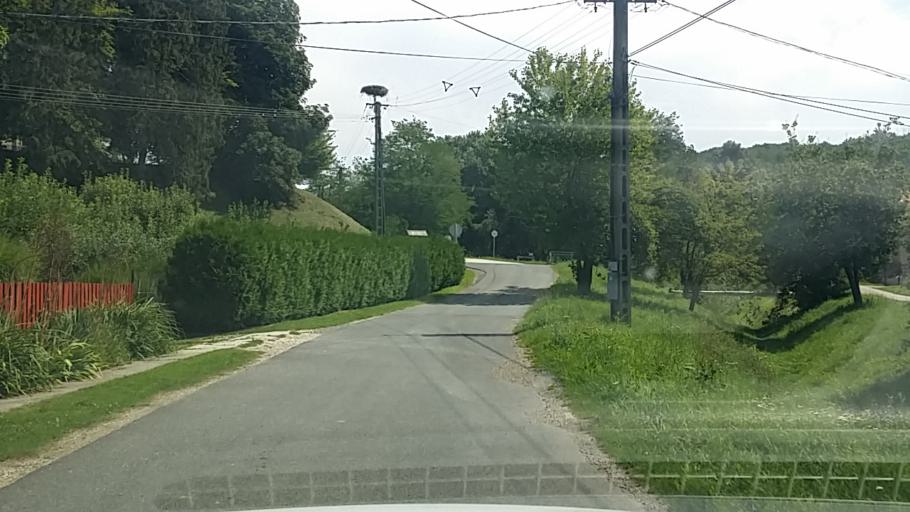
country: HU
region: Zala
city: Letenye
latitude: 46.4570
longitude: 16.6733
